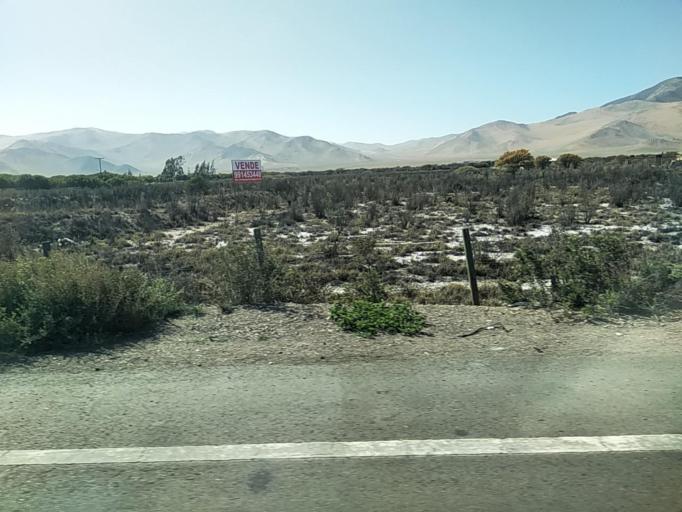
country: CL
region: Atacama
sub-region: Provincia de Copiapo
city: Copiapo
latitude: -27.3410
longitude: -70.6096
